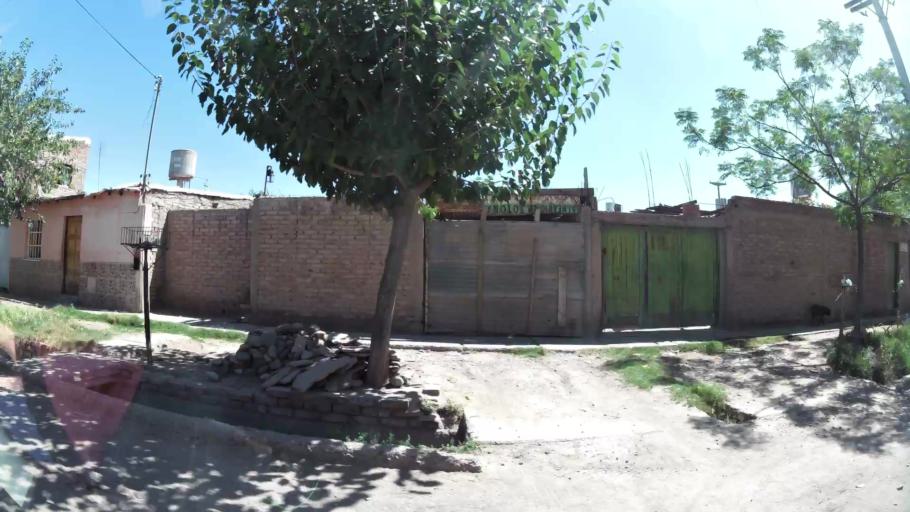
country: AR
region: Mendoza
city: Villa Nueva
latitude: -32.8761
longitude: -68.7970
